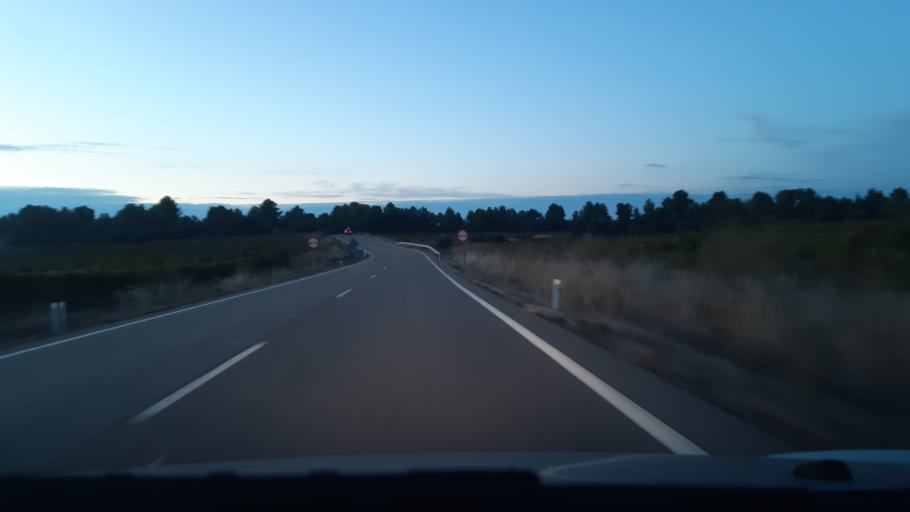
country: ES
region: Aragon
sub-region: Provincia de Teruel
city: Calaceite
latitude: 40.9603
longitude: 0.2140
